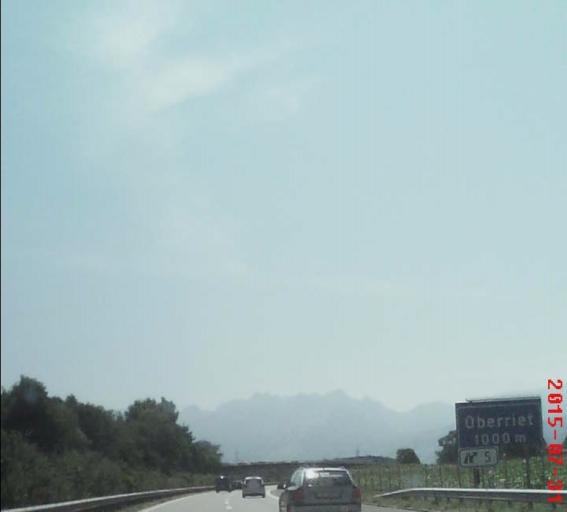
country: CH
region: Saint Gallen
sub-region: Wahlkreis Rheintal
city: Oberriet
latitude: 47.3178
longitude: 9.5848
